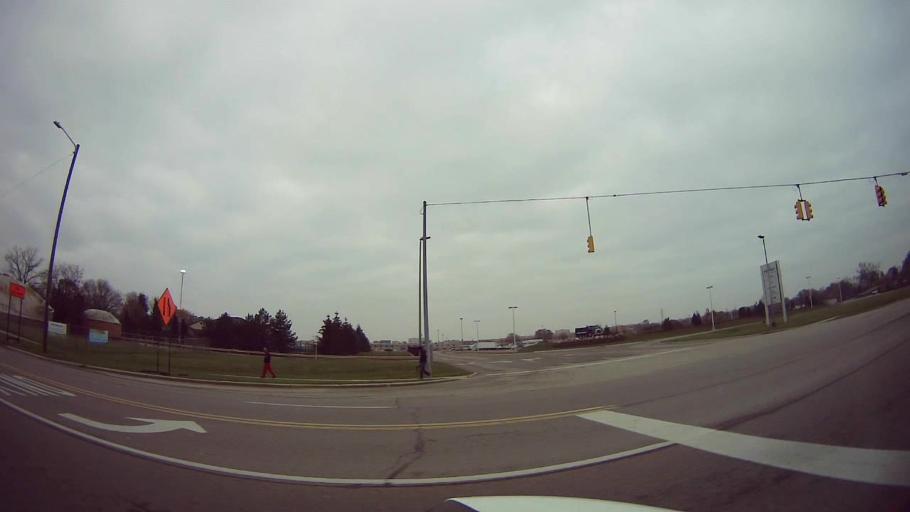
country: US
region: Michigan
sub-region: Wayne County
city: Redford
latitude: 42.3762
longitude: -83.2610
